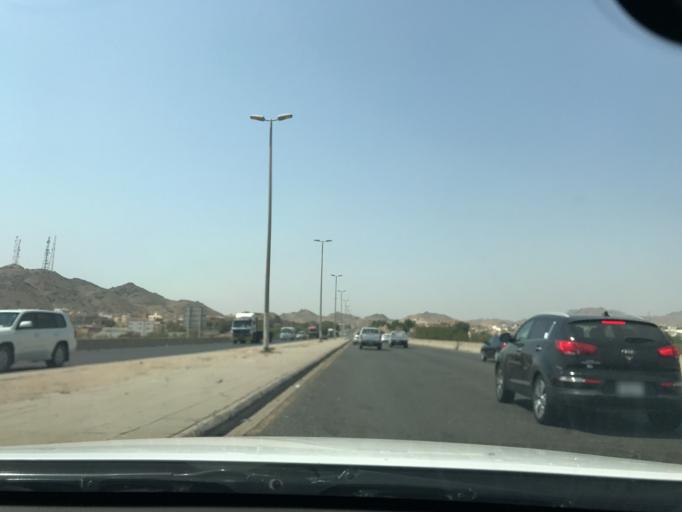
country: SA
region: Makkah
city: Jeddah
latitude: 21.3895
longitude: 39.4269
